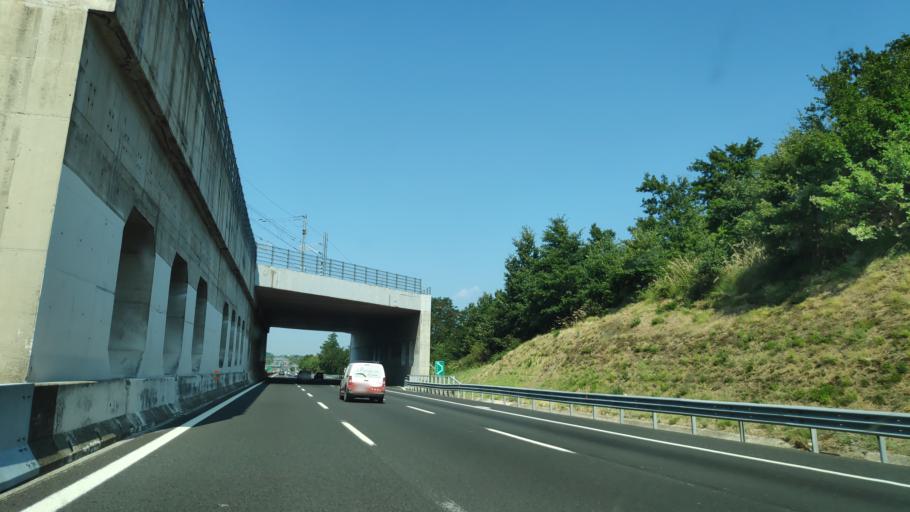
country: IT
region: Campania
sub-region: Provincia di Caserta
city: Bivio Mortola
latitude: 41.4234
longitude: 13.9221
